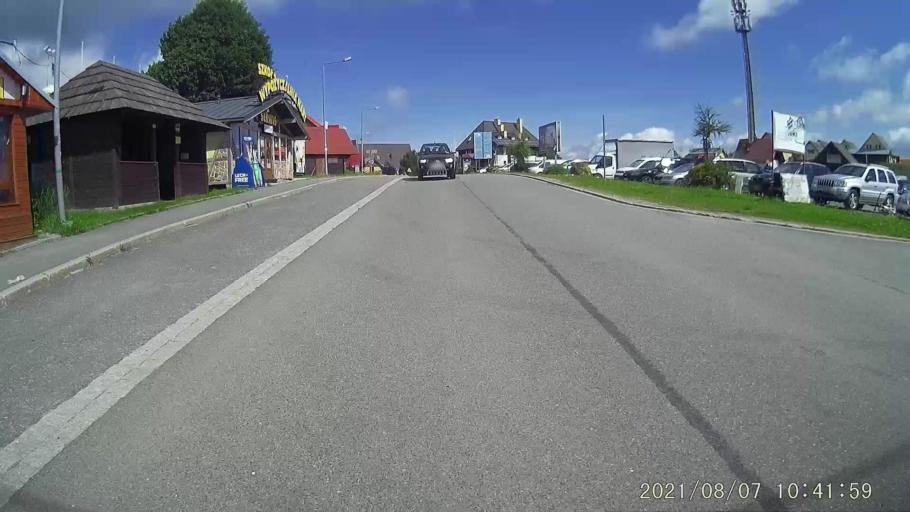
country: PL
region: Lower Silesian Voivodeship
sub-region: Powiat klodzki
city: Duszniki-Zdroj
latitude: 50.3349
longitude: 16.3891
